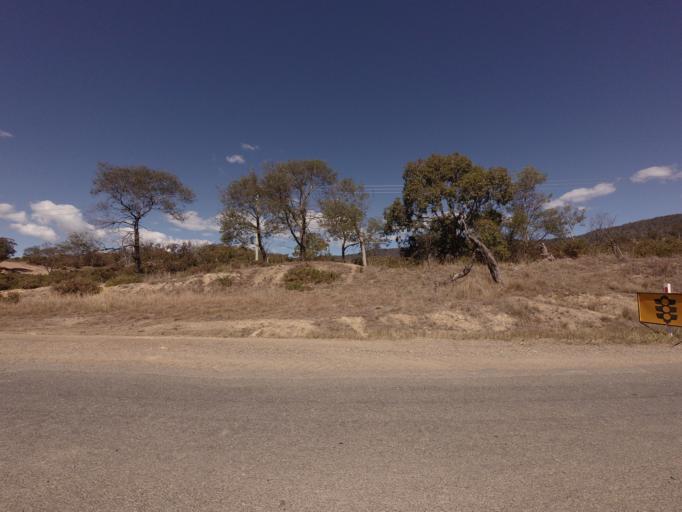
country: AU
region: Tasmania
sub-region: Break O'Day
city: St Helens
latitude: -41.6493
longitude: 147.9345
